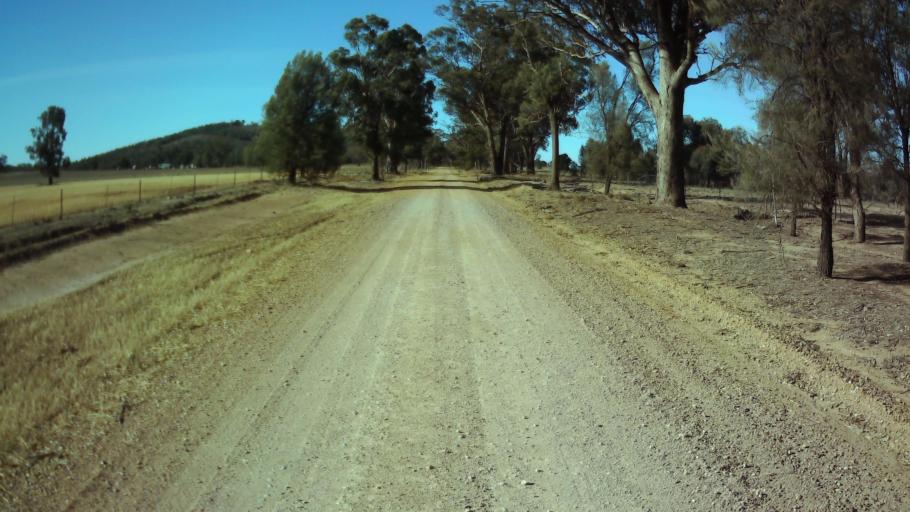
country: AU
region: New South Wales
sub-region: Weddin
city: Grenfell
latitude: -33.7998
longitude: 147.8793
